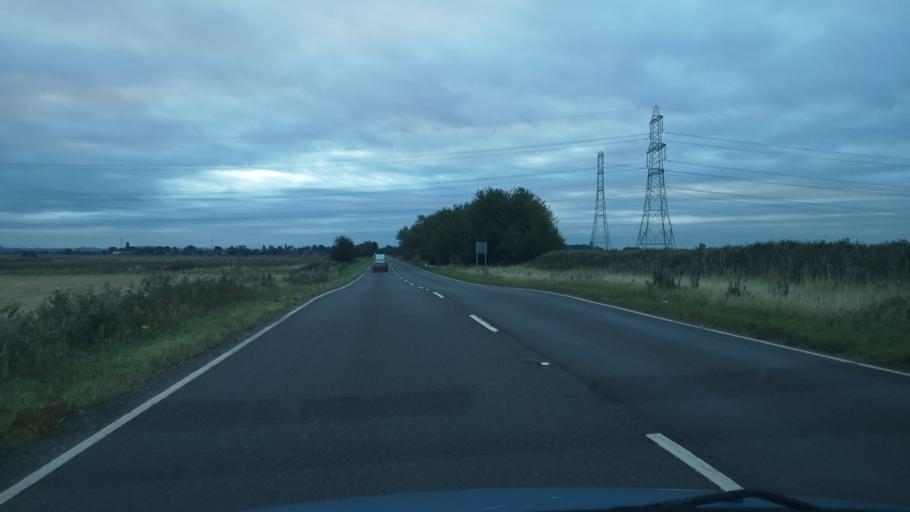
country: GB
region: England
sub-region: North Lincolnshire
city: Gunness
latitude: 53.5779
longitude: -0.7647
